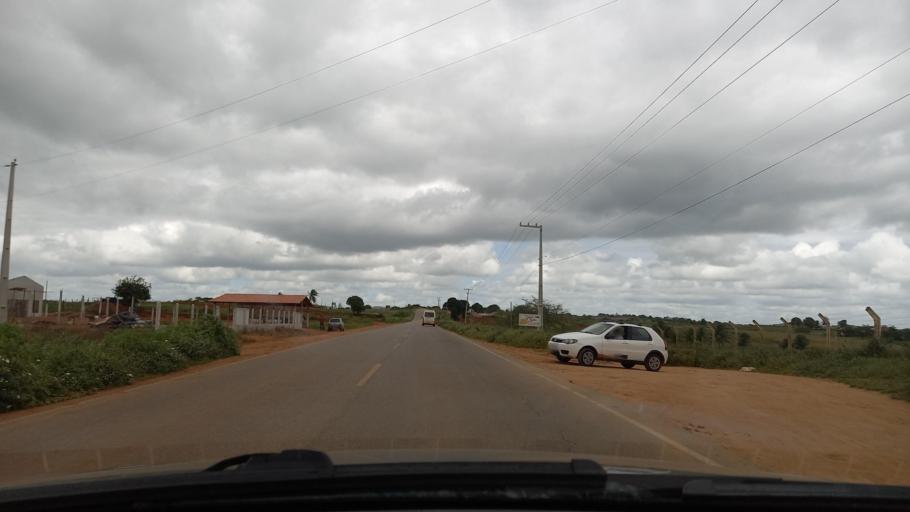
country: BR
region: Sergipe
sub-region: Caninde De Sao Francisco
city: Caninde de Sao Francisco
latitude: -9.6734
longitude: -37.8005
